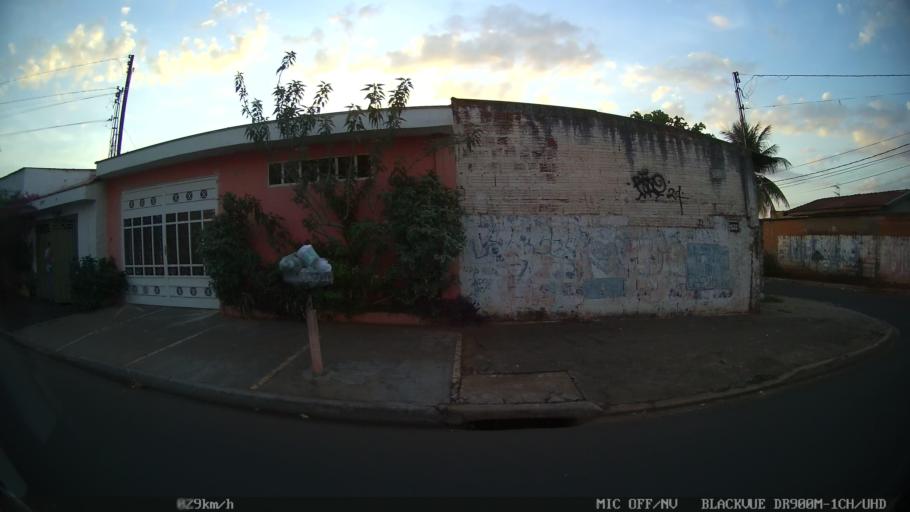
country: BR
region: Sao Paulo
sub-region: Ribeirao Preto
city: Ribeirao Preto
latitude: -21.1395
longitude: -47.8219
